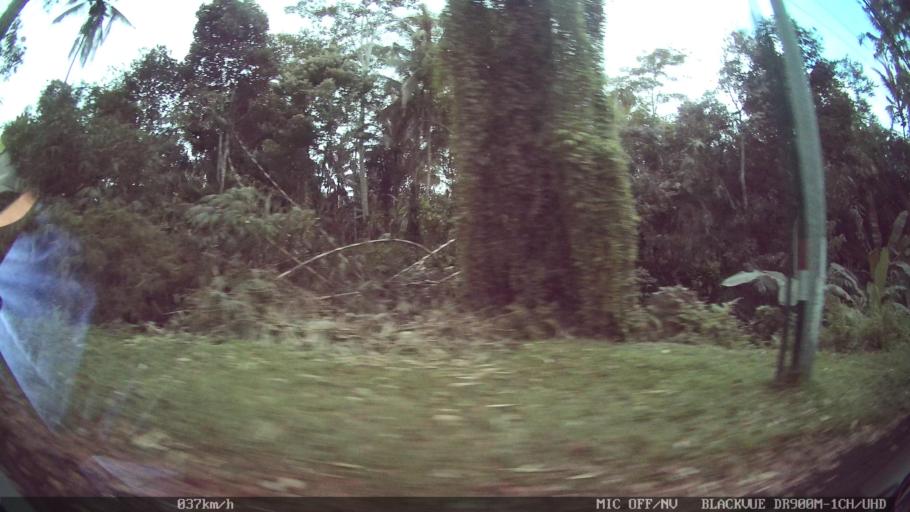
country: ID
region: Bali
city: Petang
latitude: -8.4115
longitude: 115.2240
